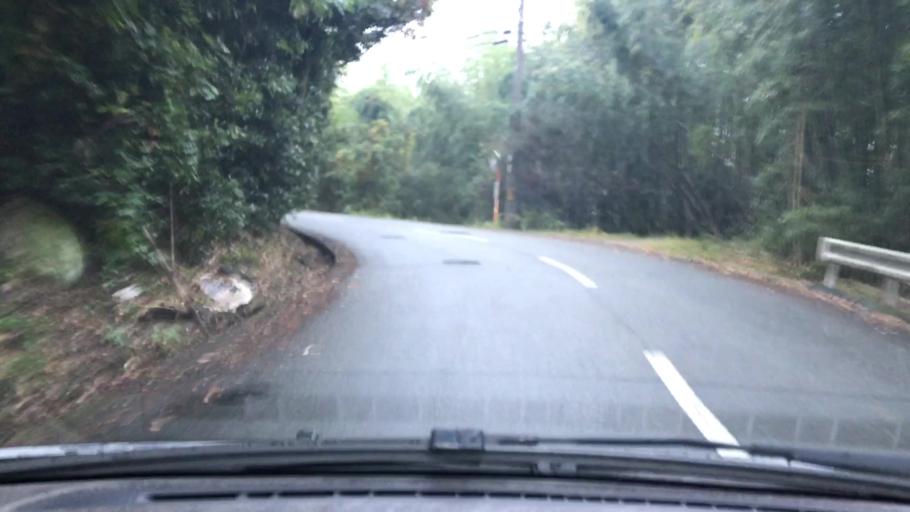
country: JP
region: Hyogo
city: Takarazuka
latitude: 34.8317
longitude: 135.2968
